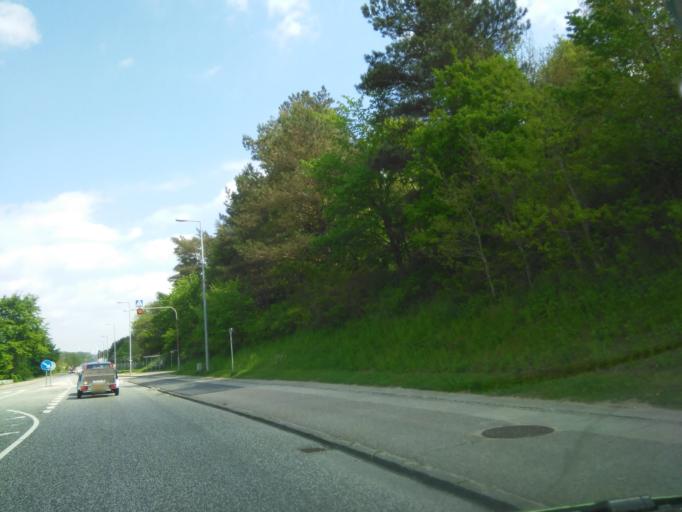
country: DK
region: Central Jutland
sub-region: Skanderborg Kommune
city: Skanderborg
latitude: 56.0357
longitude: 9.9054
